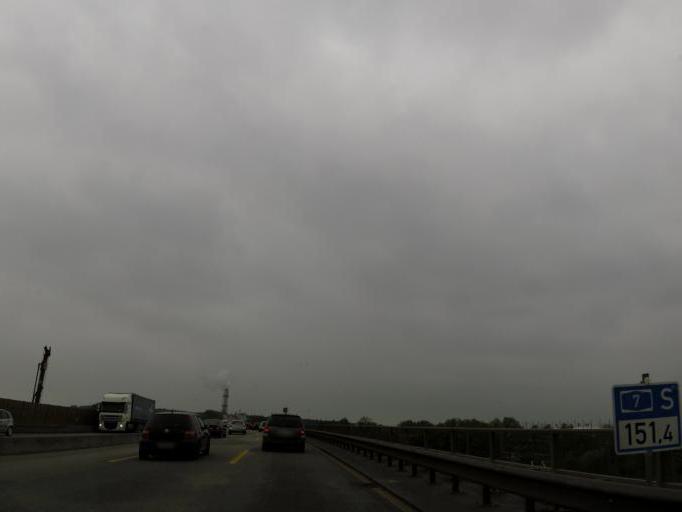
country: DE
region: Hamburg
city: Stellingen
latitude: 53.5911
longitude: 9.9174
